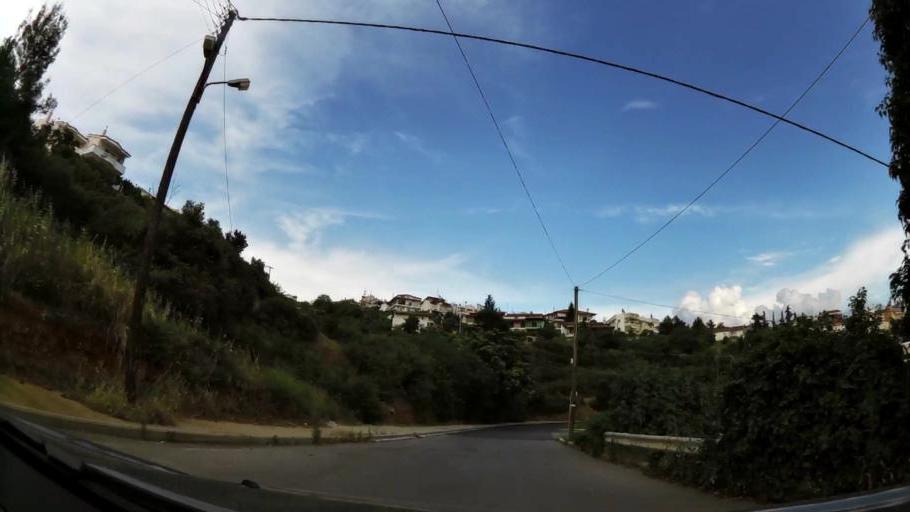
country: GR
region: Central Macedonia
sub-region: Nomos Thessalonikis
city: Pefka
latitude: 40.6586
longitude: 22.9967
